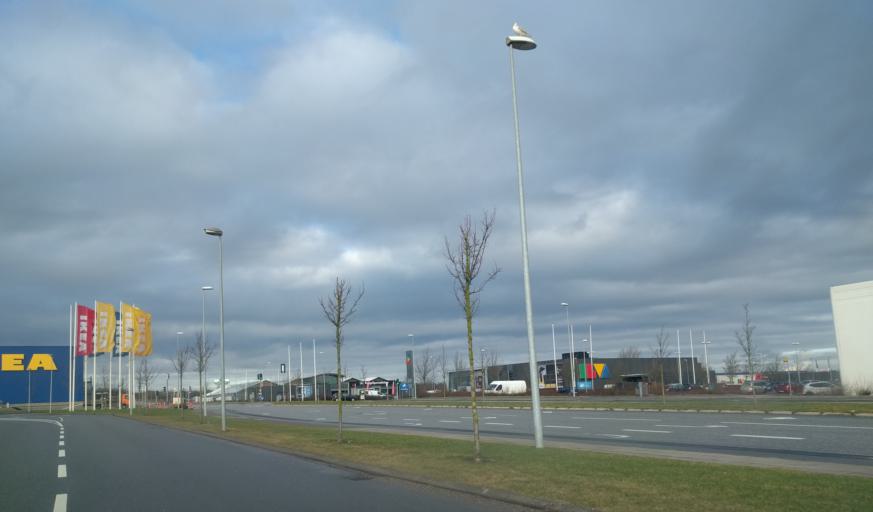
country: DK
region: North Denmark
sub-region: Alborg Kommune
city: Svenstrup
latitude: 56.9957
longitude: 9.8684
